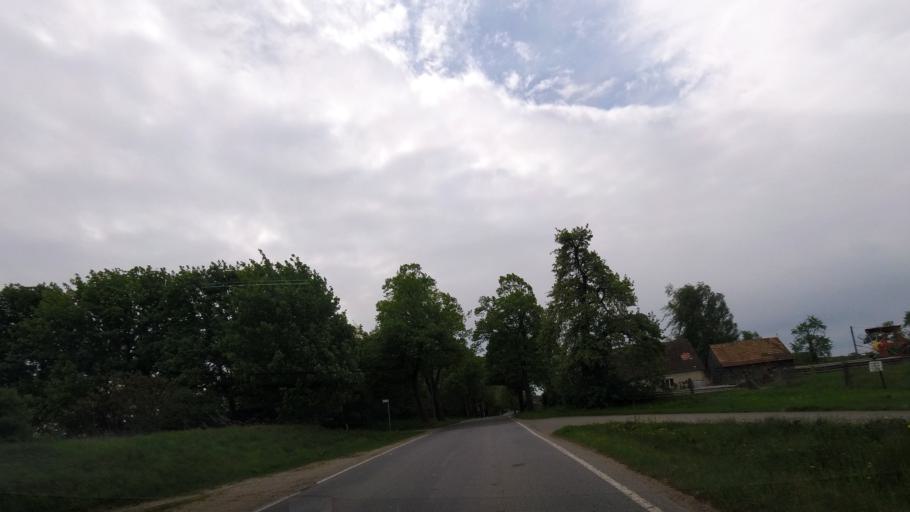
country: DE
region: Brandenburg
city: Dahme
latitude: 51.9035
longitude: 13.4076
